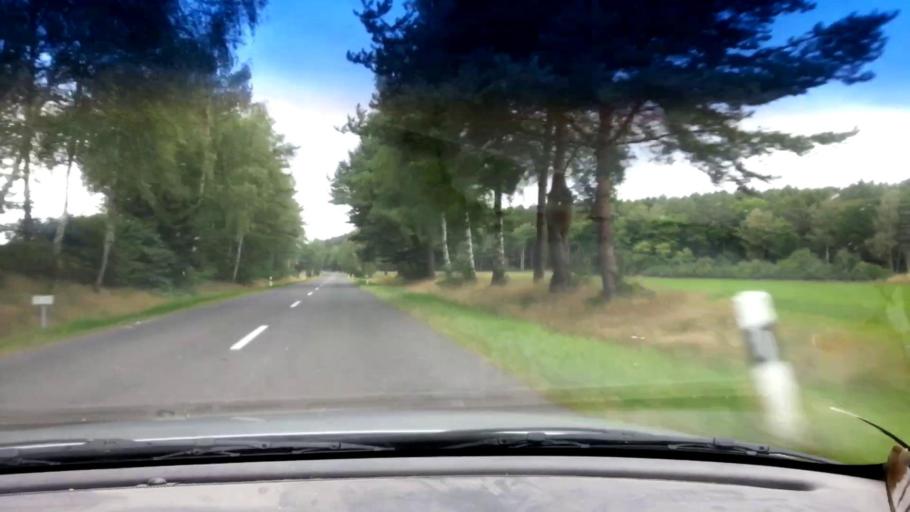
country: DE
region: Bavaria
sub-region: Upper Palatinate
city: Waldsassen
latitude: 50.0308
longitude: 12.3139
